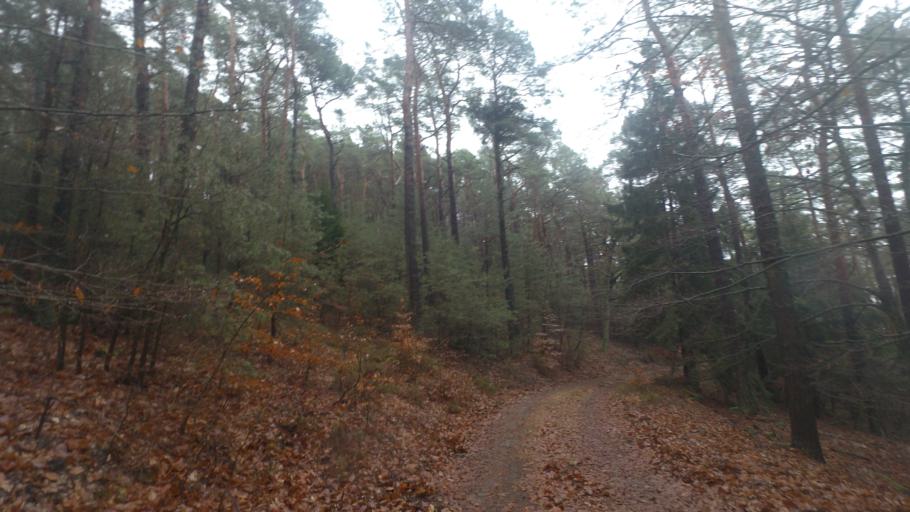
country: DE
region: Rheinland-Pfalz
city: Lindenberg
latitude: 49.3952
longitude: 8.1329
